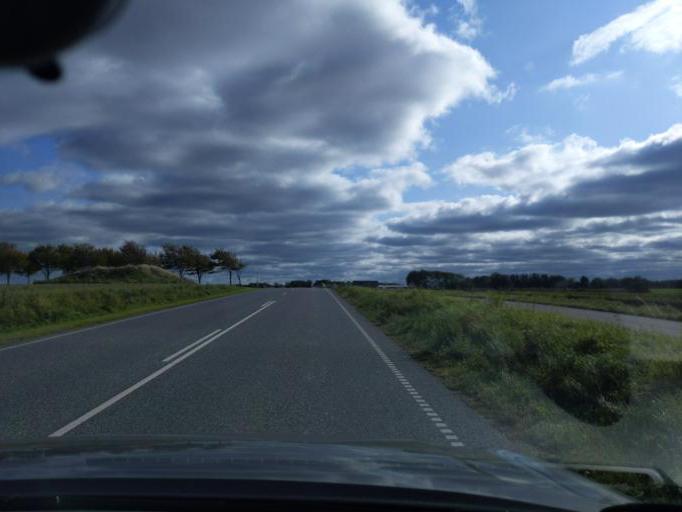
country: DK
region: North Denmark
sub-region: Mariagerfjord Kommune
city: Hobro
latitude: 56.5206
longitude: 9.7332
